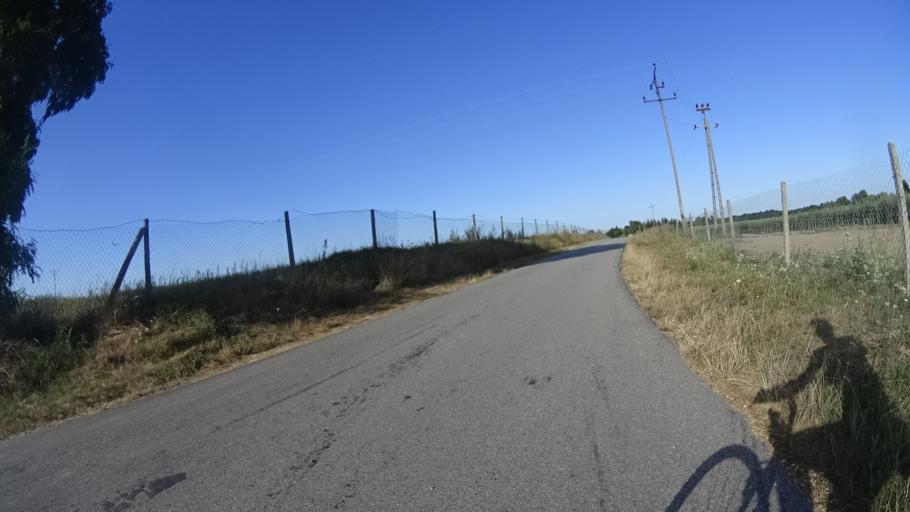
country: PL
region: Masovian Voivodeship
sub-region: Powiat grojecki
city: Goszczyn
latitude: 51.6814
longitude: 20.8256
